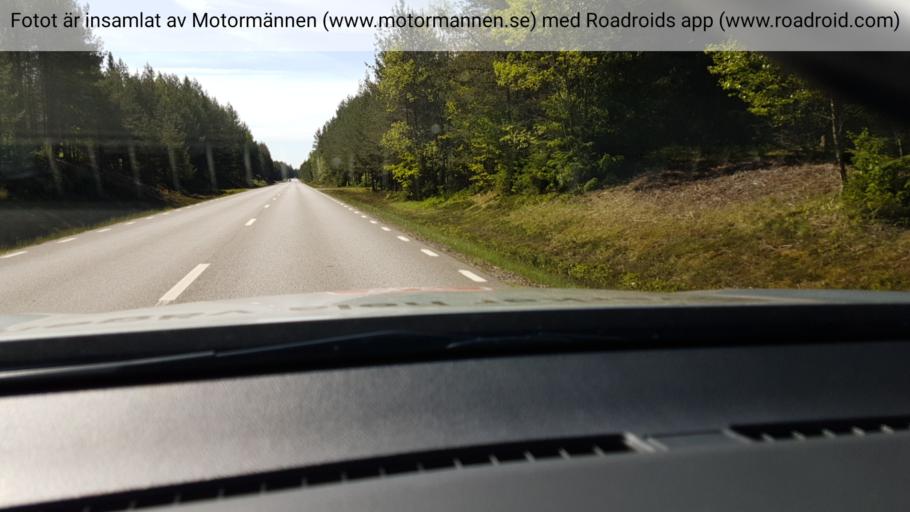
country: SE
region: Vaestra Goetaland
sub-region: Hjo Kommun
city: Hjo
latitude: 58.3528
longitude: 14.2189
